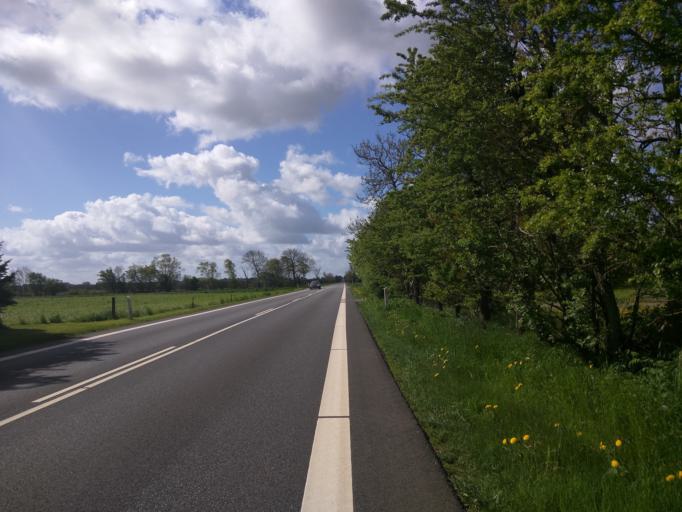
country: DK
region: Central Jutland
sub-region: Viborg Kommune
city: Viborg
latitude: 56.3778
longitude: 9.4419
